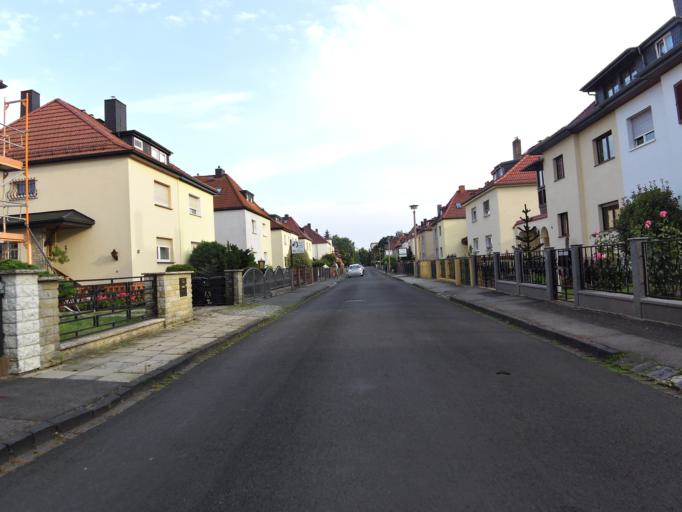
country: DE
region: Saxony
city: Leipzig
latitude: 51.3606
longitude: 12.4220
